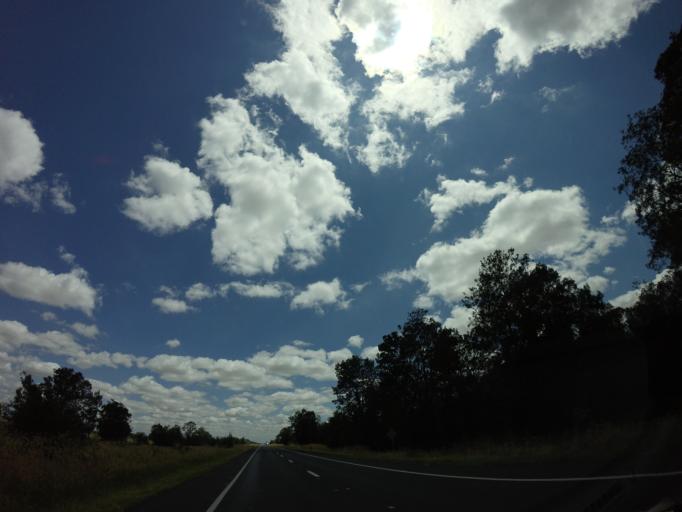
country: AU
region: New South Wales
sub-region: Moree Plains
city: Moree
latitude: -29.0715
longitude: 150.0433
